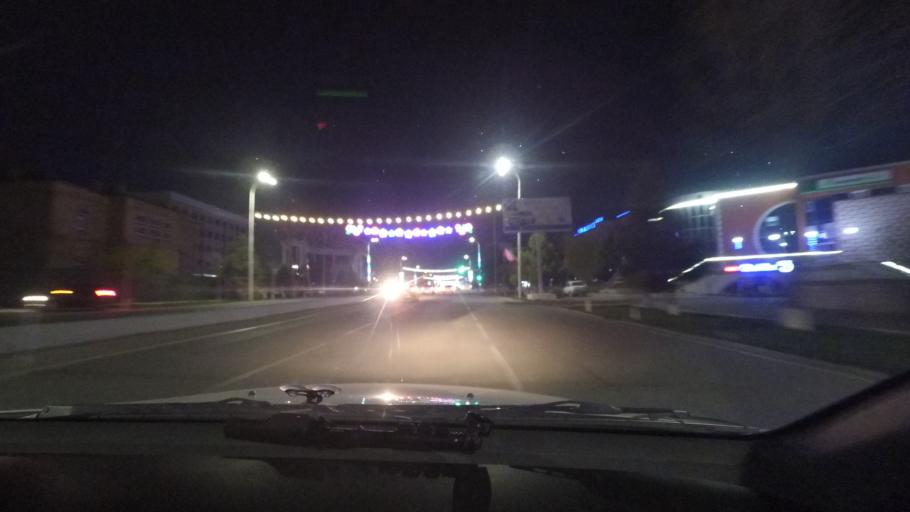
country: UZ
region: Bukhara
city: Bukhara
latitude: 39.7708
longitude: 64.4462
